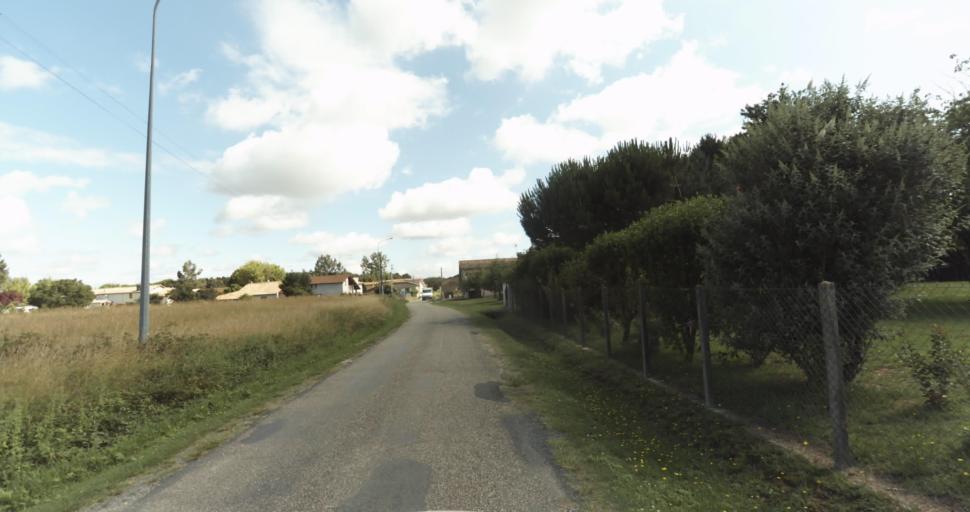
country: FR
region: Aquitaine
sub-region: Departement de la Gironde
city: Bazas
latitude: 44.4415
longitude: -0.1936
